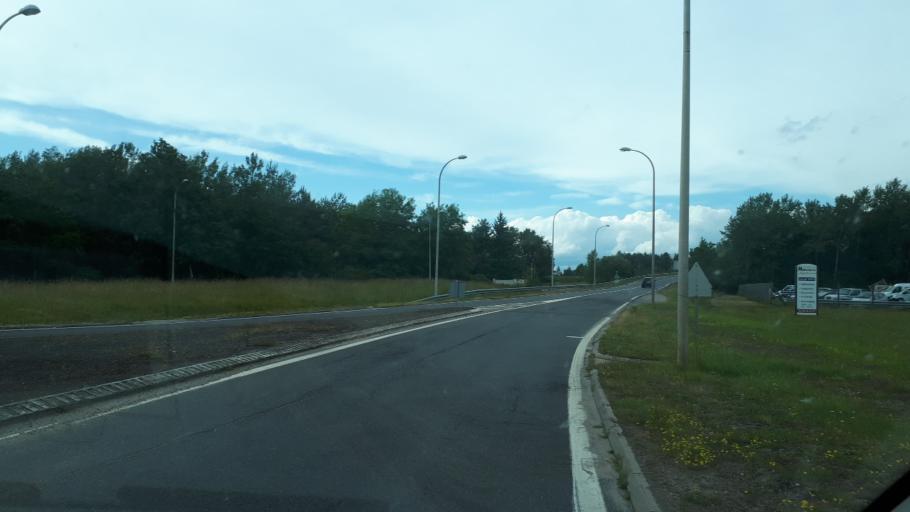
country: FR
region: Centre
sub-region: Departement du Loir-et-Cher
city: Villefranche-sur-Cher
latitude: 47.3188
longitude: 1.7606
